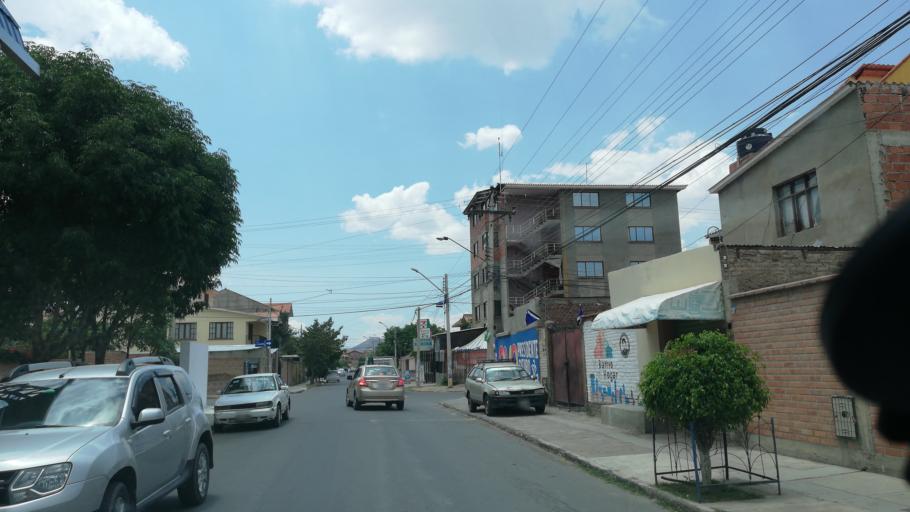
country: BO
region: Cochabamba
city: Cochabamba
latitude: -17.3780
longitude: -66.1946
